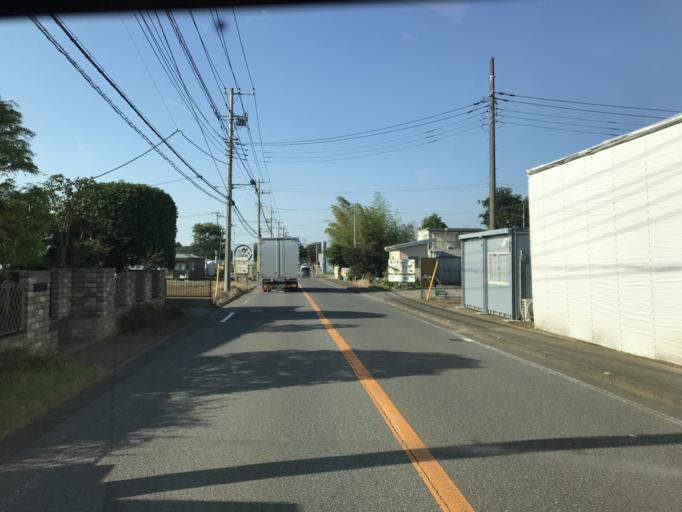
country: JP
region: Chiba
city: Chiba
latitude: 35.5641
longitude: 140.2024
